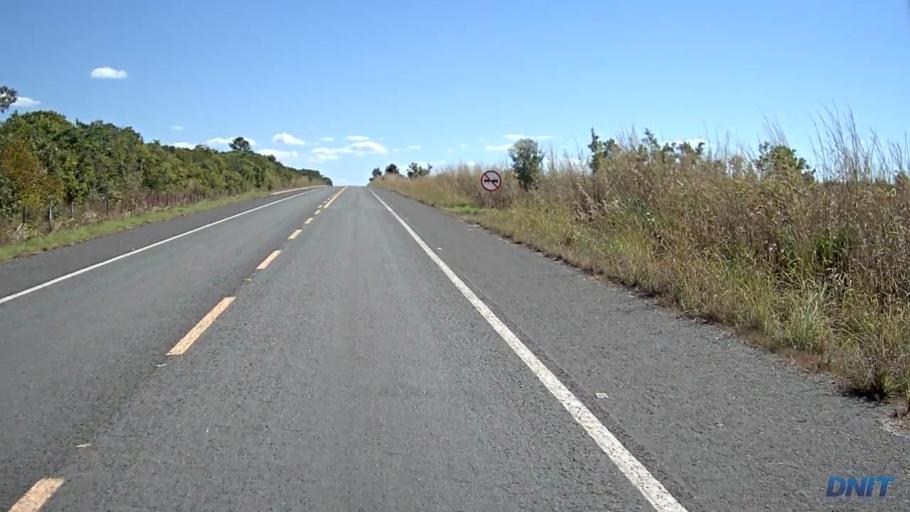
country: BR
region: Goias
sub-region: Sao Miguel Do Araguaia
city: Sao Miguel do Araguaia
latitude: -13.2931
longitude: -50.3933
